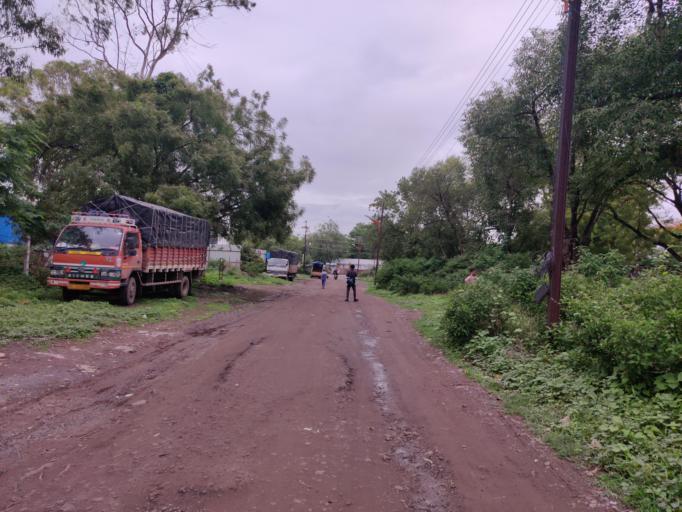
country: IN
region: Maharashtra
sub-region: Aurangabad Division
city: Aurangabad
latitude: 19.8777
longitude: 75.3790
